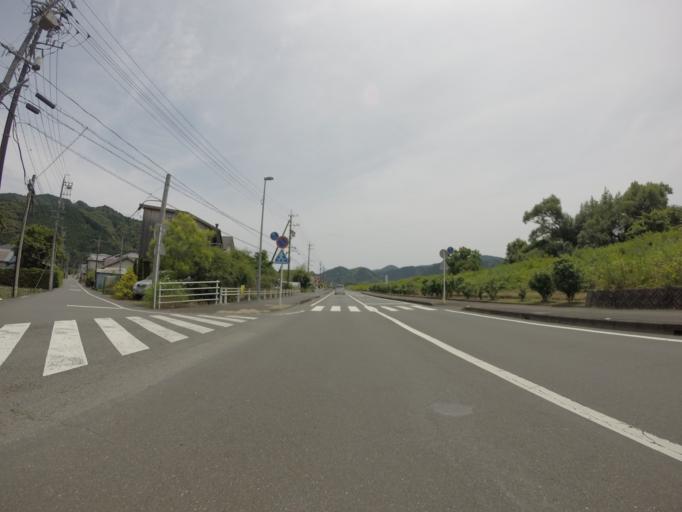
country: JP
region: Shizuoka
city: Shizuoka-shi
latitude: 34.9879
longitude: 138.3040
